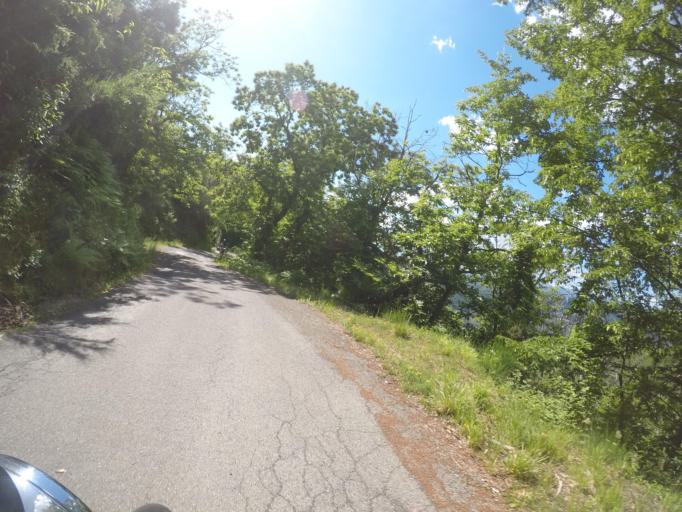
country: IT
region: Tuscany
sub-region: Provincia di Massa-Carrara
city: Casola in Lunigiana
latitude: 44.1787
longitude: 10.1626
